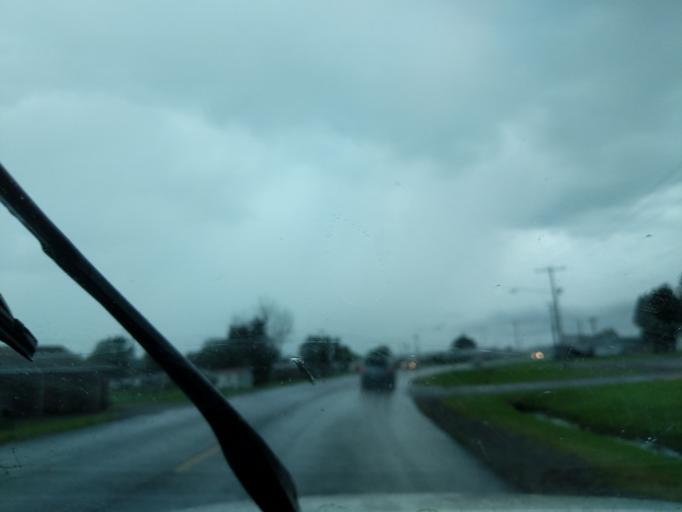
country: US
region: Missouri
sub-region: New Madrid County
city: New Madrid
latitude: 36.5963
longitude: -89.5340
